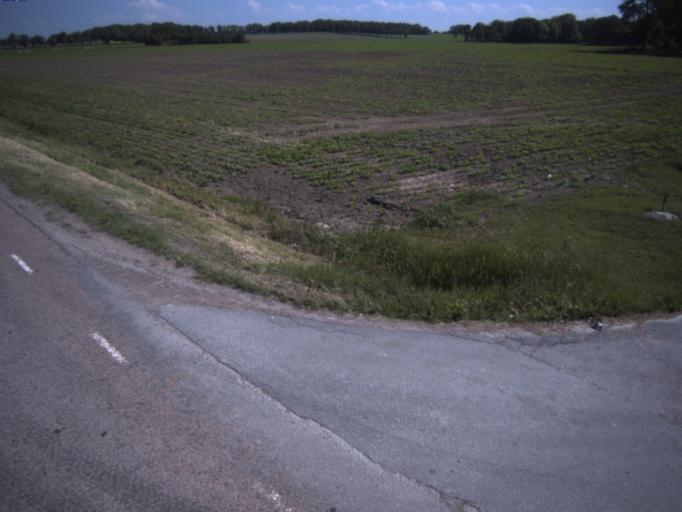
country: SE
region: Skane
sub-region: Helsingborg
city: Barslov
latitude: 56.0325
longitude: 12.7906
